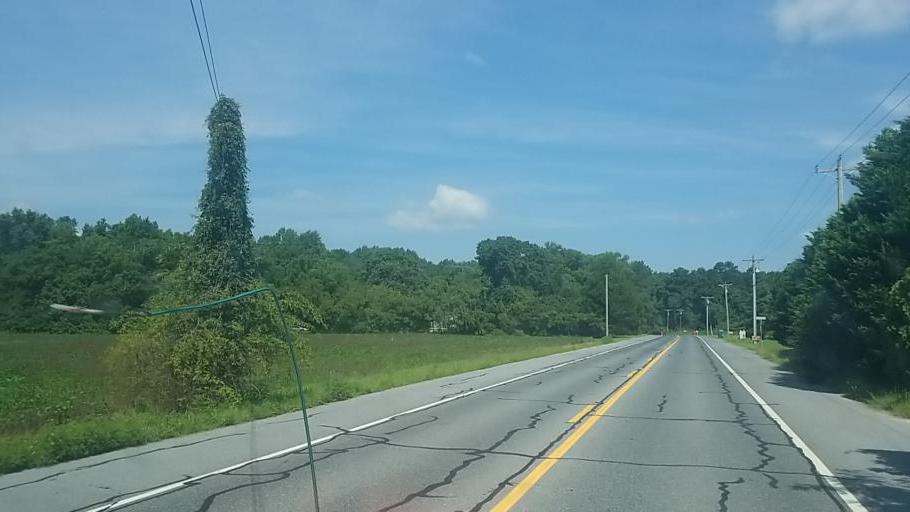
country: US
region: Delaware
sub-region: Sussex County
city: Seaford
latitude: 38.6733
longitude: -75.5751
